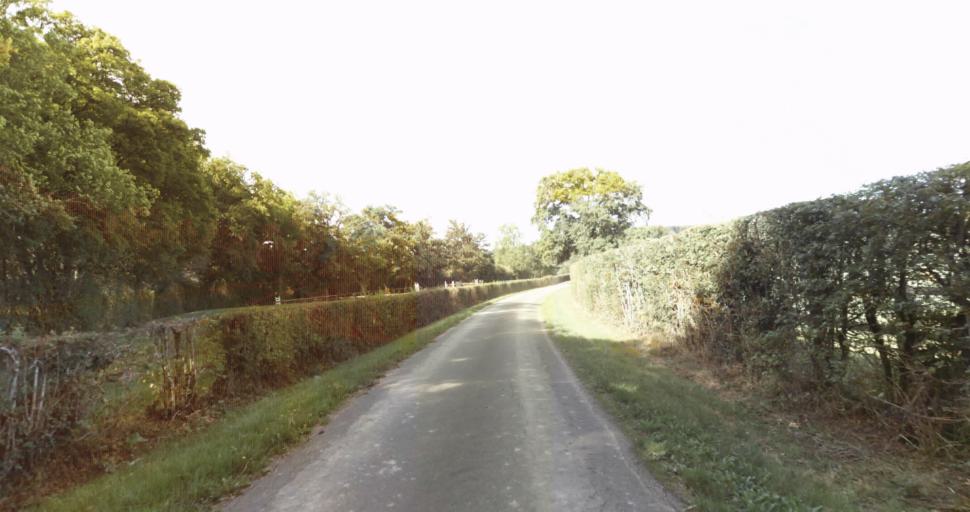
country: FR
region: Lower Normandy
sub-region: Departement de l'Orne
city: Sees
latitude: 48.7035
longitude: 0.1765
